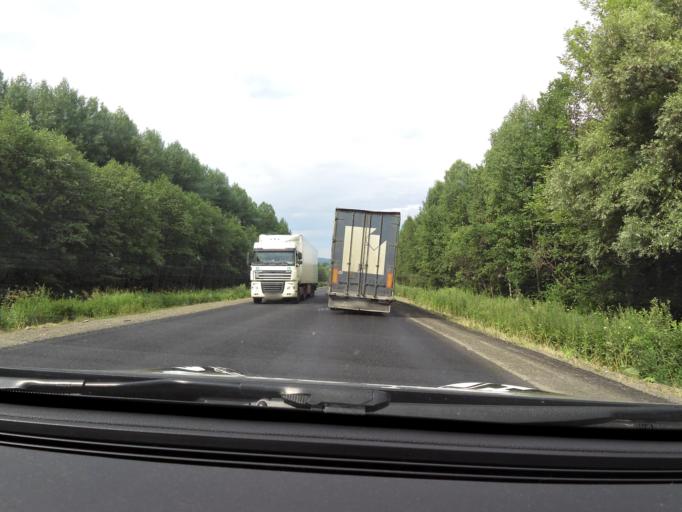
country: RU
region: Chelyabinsk
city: Asha
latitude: 54.8598
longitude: 57.1549
